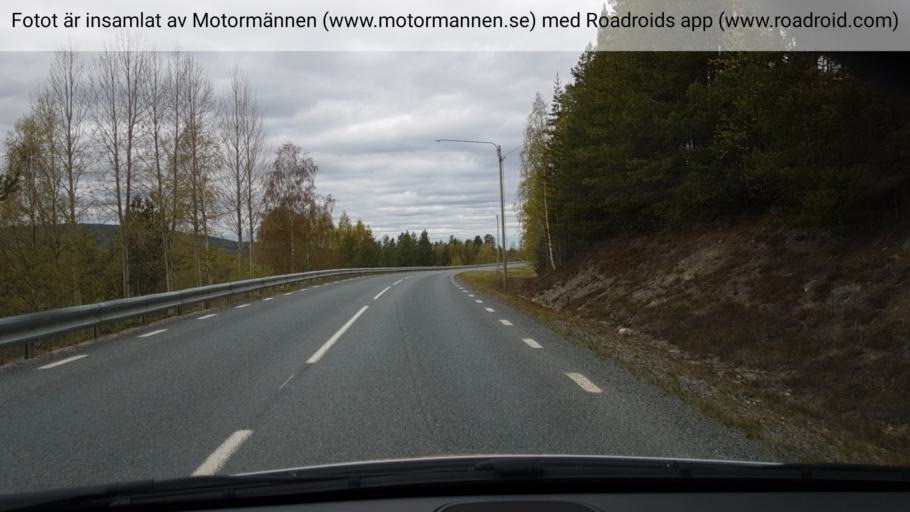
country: SE
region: Vaesterbotten
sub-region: Lycksele Kommun
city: Soderfors
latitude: 65.0982
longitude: 18.3154
